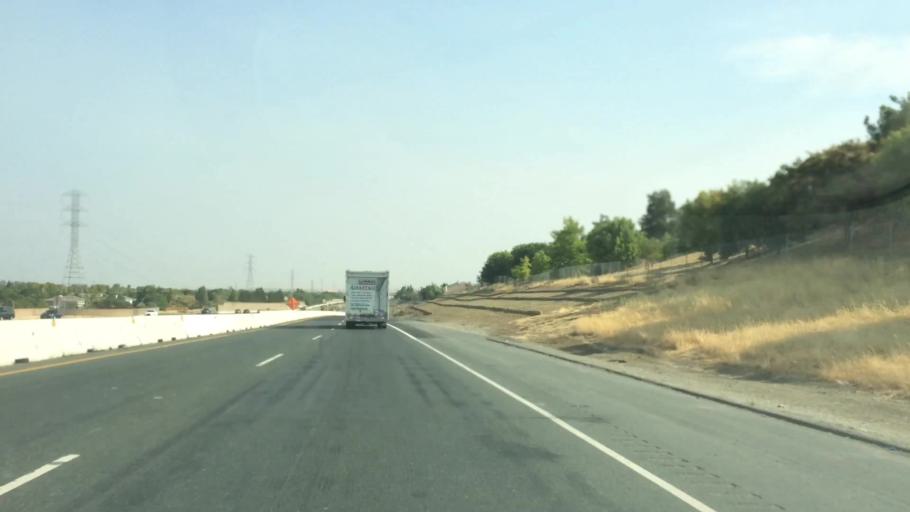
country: US
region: California
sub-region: Contra Costa County
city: Brentwood
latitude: 37.9419
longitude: -121.7413
